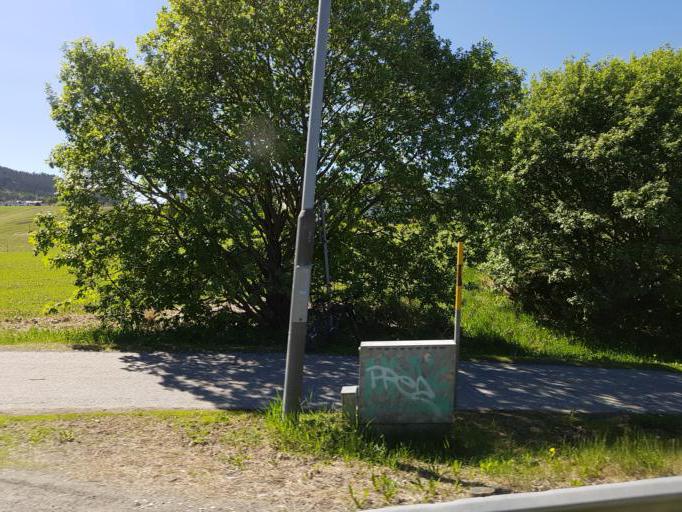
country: NO
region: Sor-Trondelag
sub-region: Trondheim
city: Trondheim
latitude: 63.4238
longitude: 10.5183
